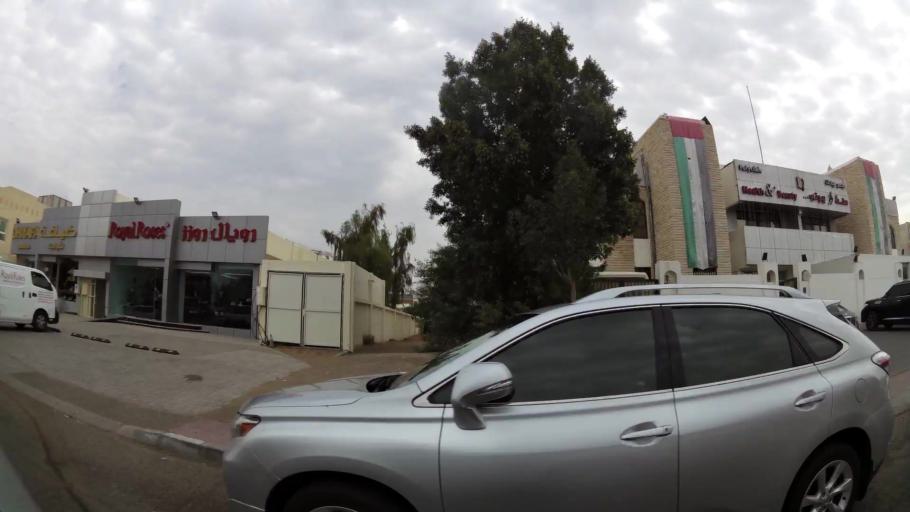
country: AE
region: Abu Dhabi
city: Al Ain
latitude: 24.2275
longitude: 55.7315
